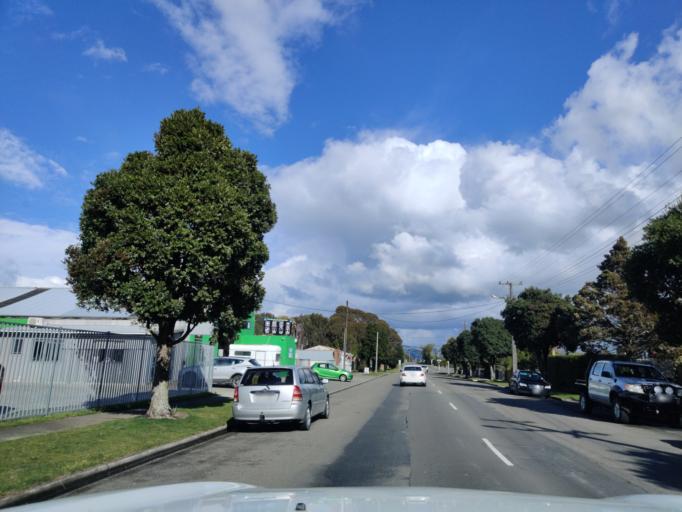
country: NZ
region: Manawatu-Wanganui
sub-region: Palmerston North City
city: Palmerston North
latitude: -40.2936
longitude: 175.7539
